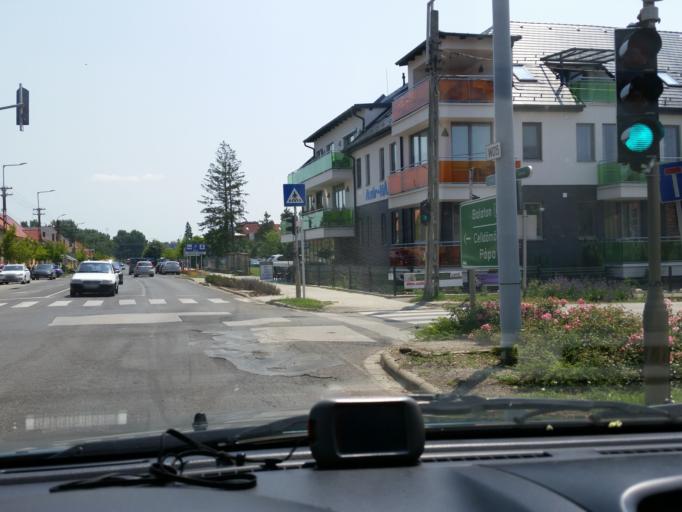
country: HU
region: Vas
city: Sarvar
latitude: 47.2495
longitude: 16.9461
